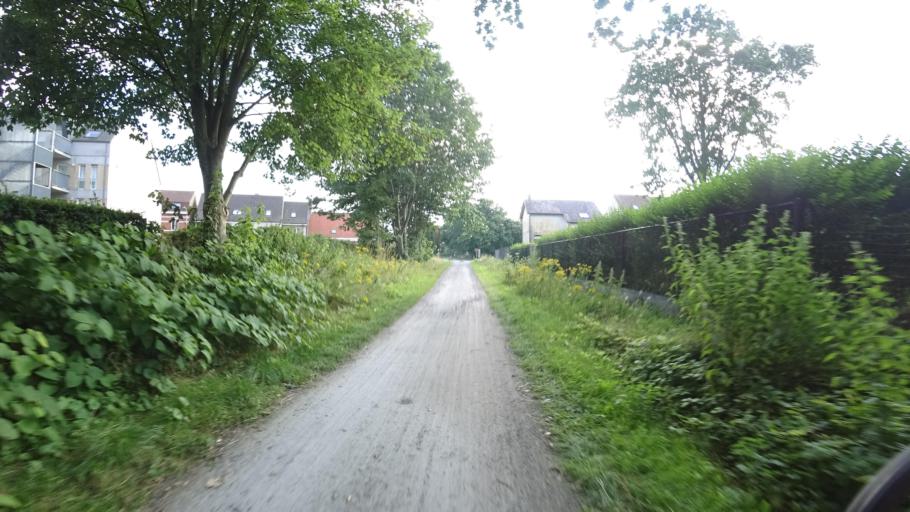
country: BE
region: Flanders
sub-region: Provincie West-Vlaanderen
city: Sint-Kruis
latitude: 51.1939
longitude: 3.2666
